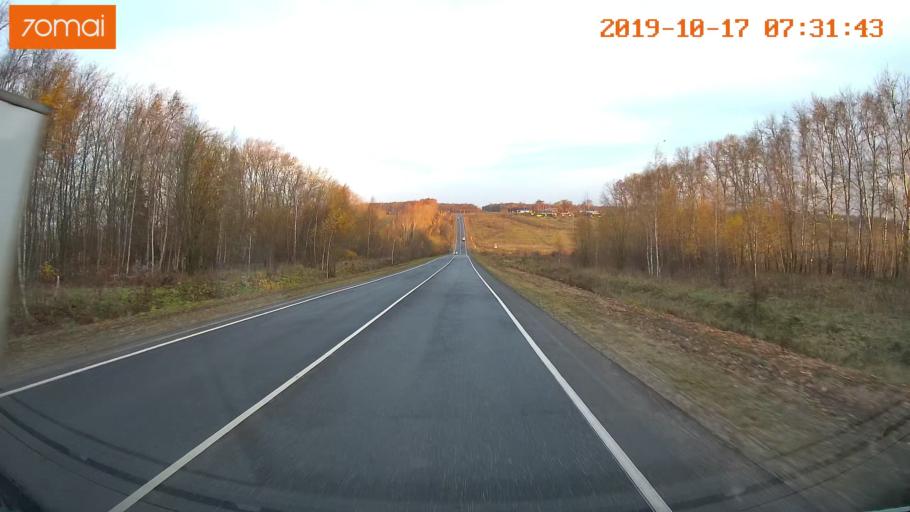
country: RU
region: Ivanovo
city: Gavrilov Posad
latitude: 56.3920
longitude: 39.9907
